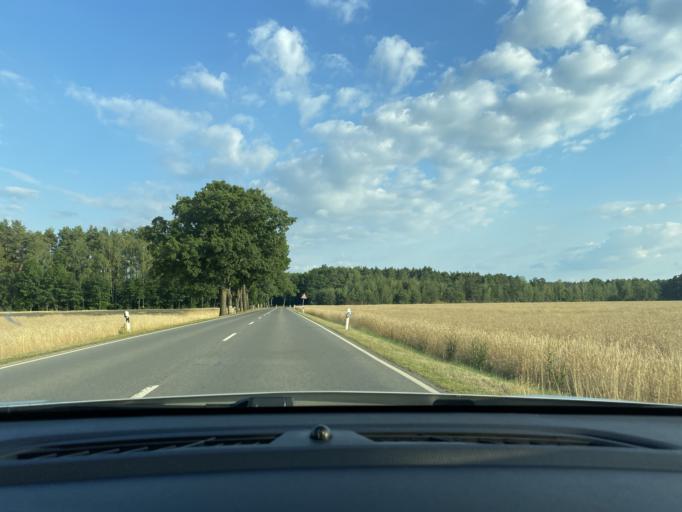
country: DE
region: Saxony
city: Wittichenau
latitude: 51.3941
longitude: 14.2957
